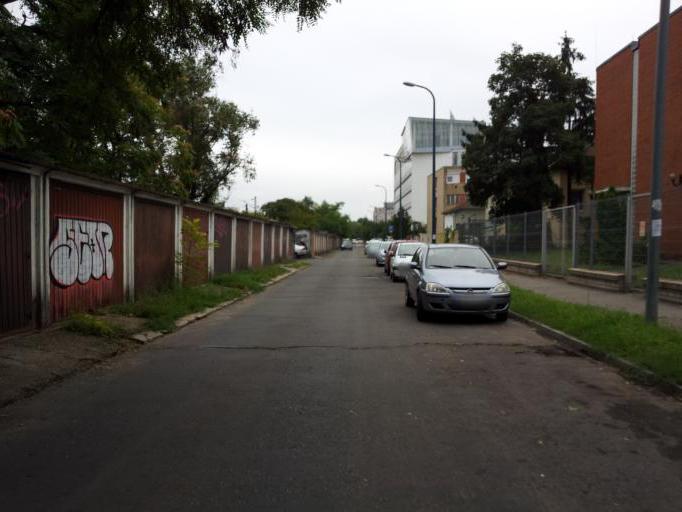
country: HU
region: Budapest
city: Budapest XIV. keruelet
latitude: 47.5157
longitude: 19.0944
